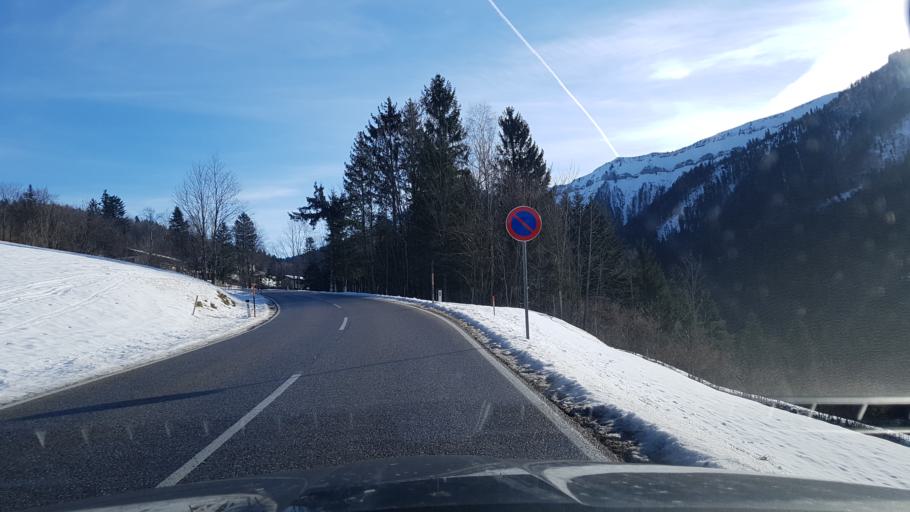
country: AT
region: Salzburg
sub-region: Politischer Bezirk Hallein
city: Krispl
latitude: 47.7080
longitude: 13.2018
